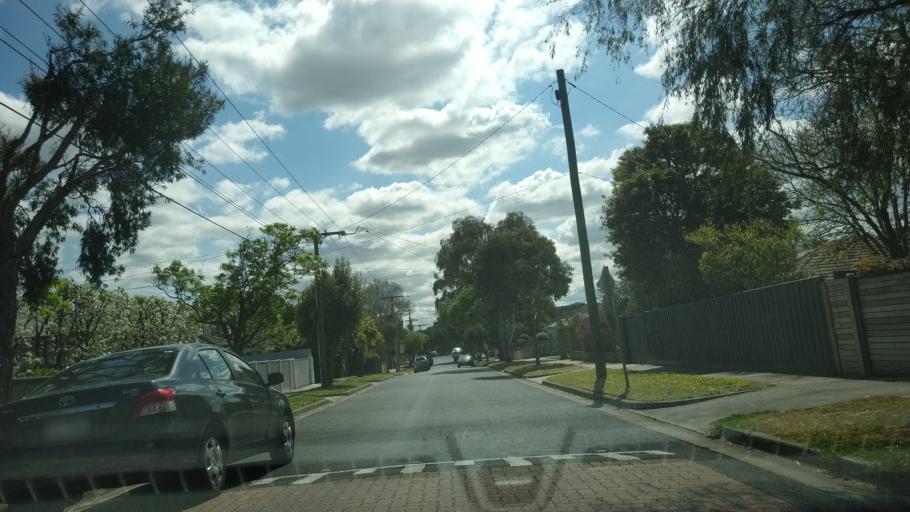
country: AU
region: Victoria
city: Highett
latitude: -37.9590
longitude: 145.0461
